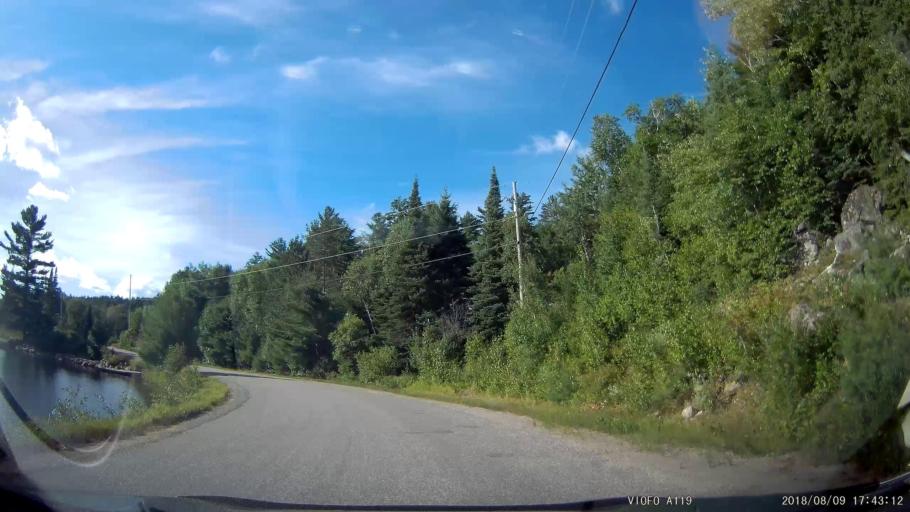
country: CA
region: Ontario
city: Rayside-Balfour
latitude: 46.6062
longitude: -81.5266
